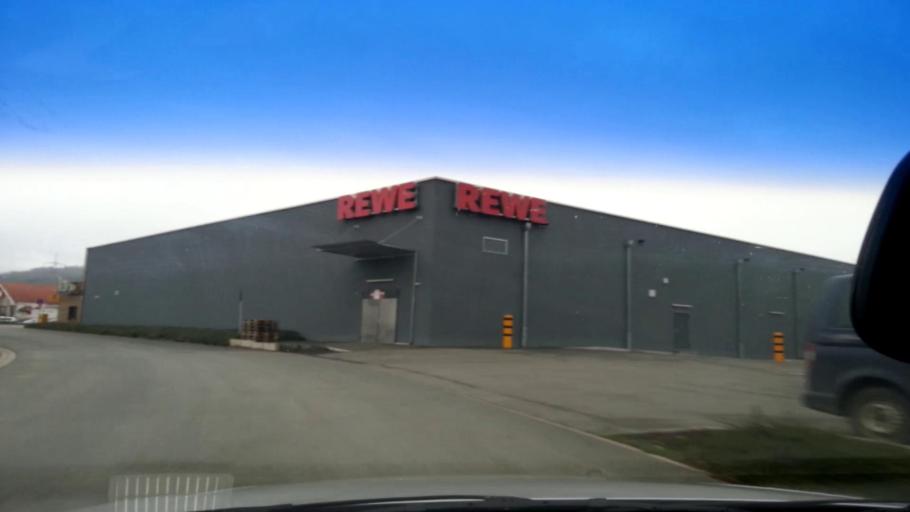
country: DE
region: Bavaria
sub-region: Upper Franconia
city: Schesslitz
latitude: 49.9706
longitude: 11.0217
